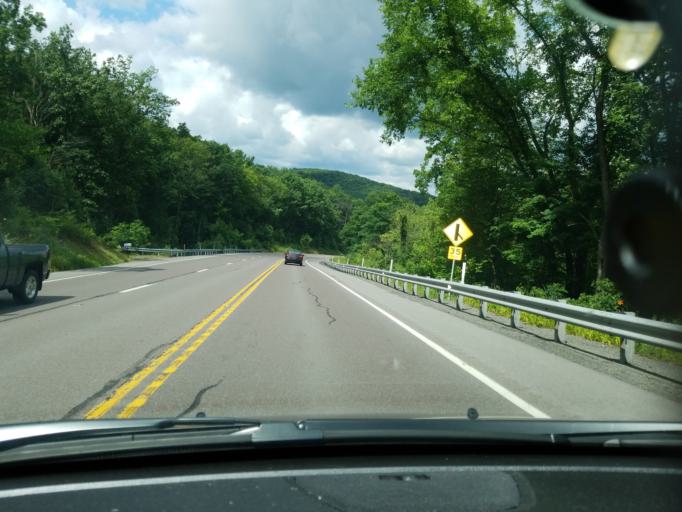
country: US
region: Pennsylvania
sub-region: Northumberland County
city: Elysburg
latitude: 40.8502
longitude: -76.5340
